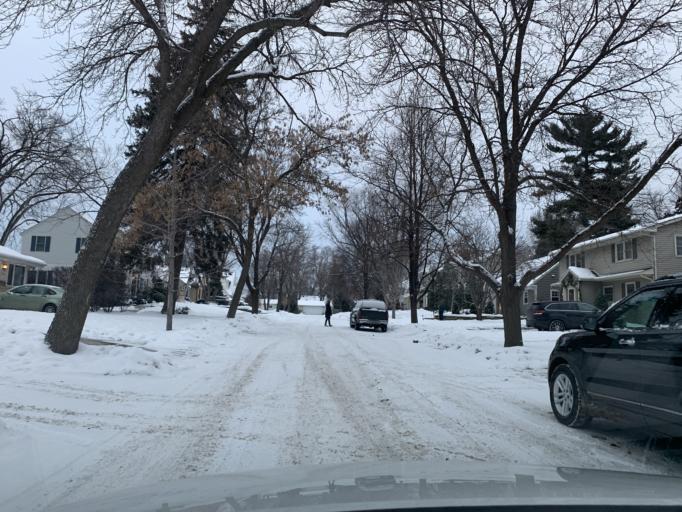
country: US
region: Minnesota
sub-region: Hennepin County
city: Saint Louis Park
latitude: 44.9283
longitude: -93.3435
